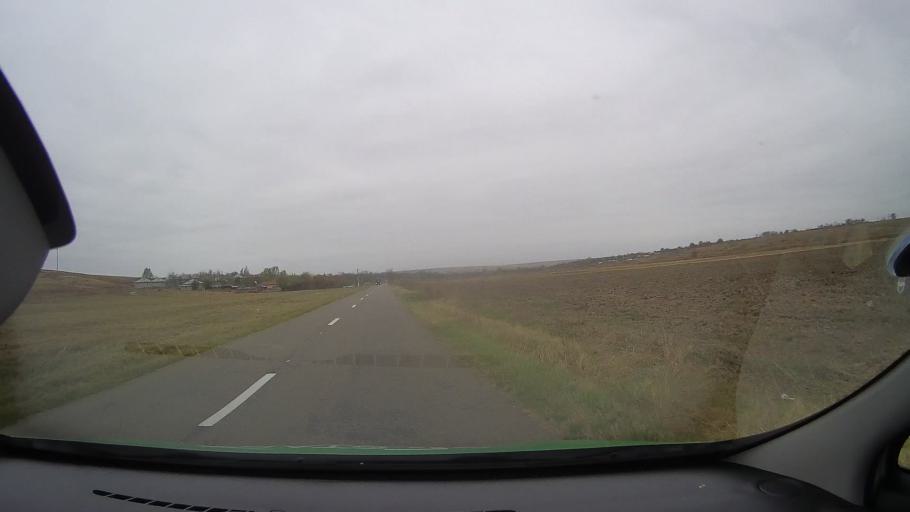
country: RO
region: Constanta
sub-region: Comuna Saraiu
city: Saraiu
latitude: 44.7250
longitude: 28.1701
